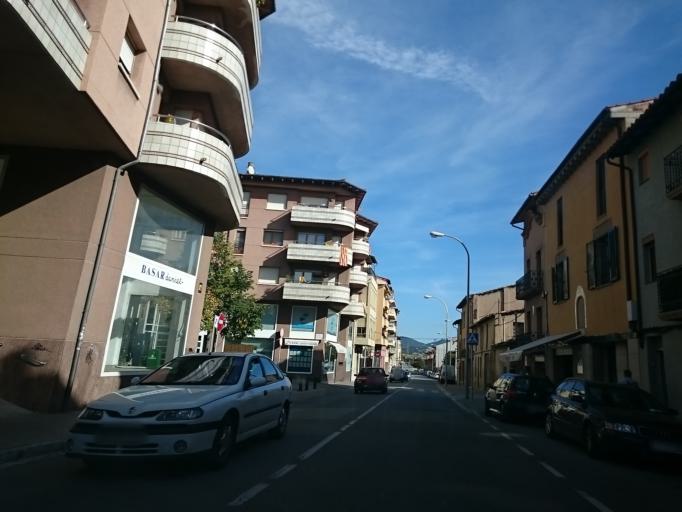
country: ES
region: Catalonia
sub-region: Provincia de Barcelona
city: Vic
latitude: 41.9287
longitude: 2.2616
